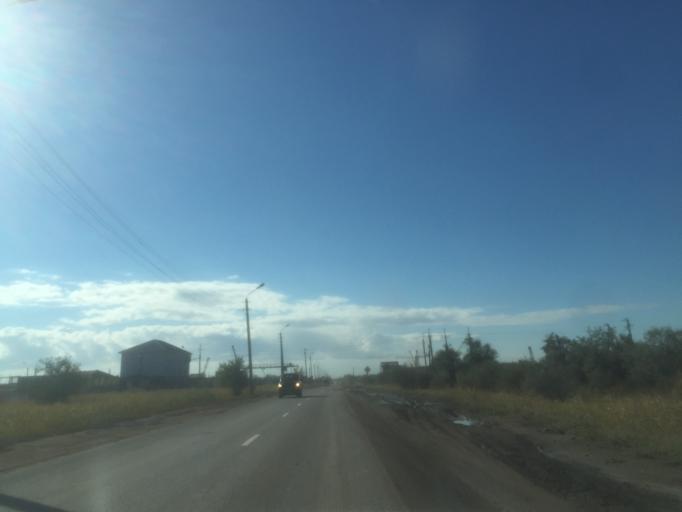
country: KZ
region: Astana Qalasy
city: Astana
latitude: 51.2105
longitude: 71.3535
